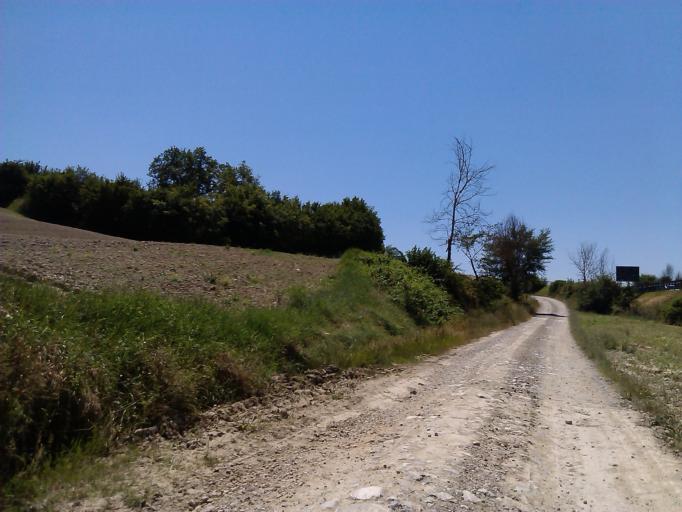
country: IT
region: Umbria
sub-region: Provincia di Terni
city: Ficulle
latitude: 42.8401
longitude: 12.0420
